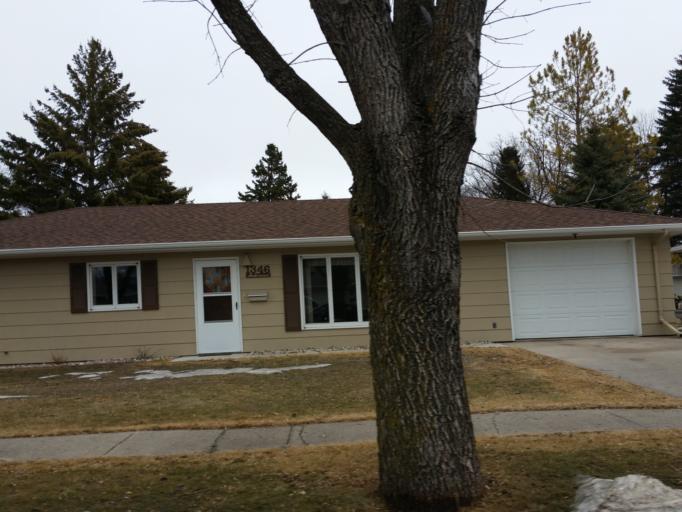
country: US
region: North Dakota
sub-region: Walsh County
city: Grafton
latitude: 48.4105
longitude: -97.4203
